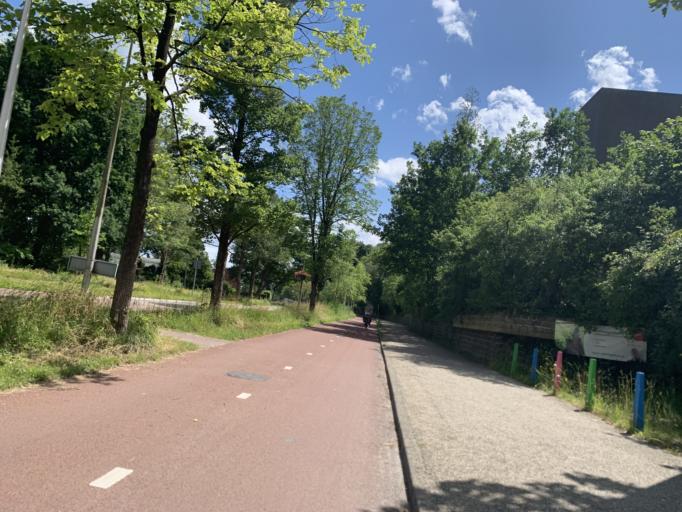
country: NL
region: Groningen
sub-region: Gemeente Haren
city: Haren
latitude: 53.1786
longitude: 6.6048
